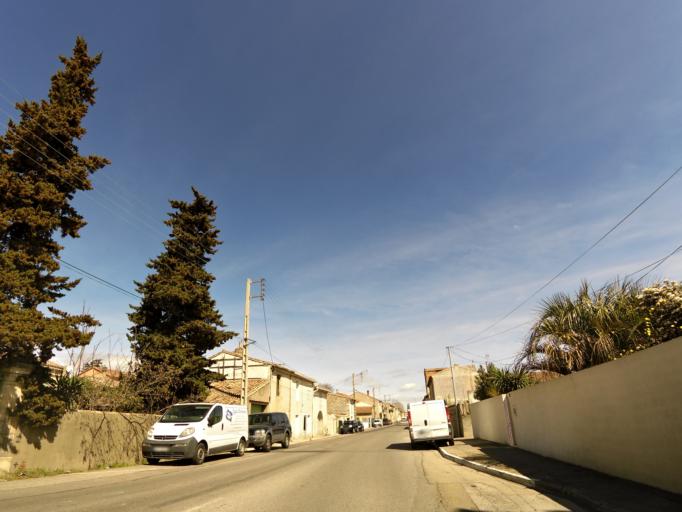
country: FR
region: Languedoc-Roussillon
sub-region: Departement du Gard
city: Milhaud
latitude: 43.7870
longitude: 4.3032
